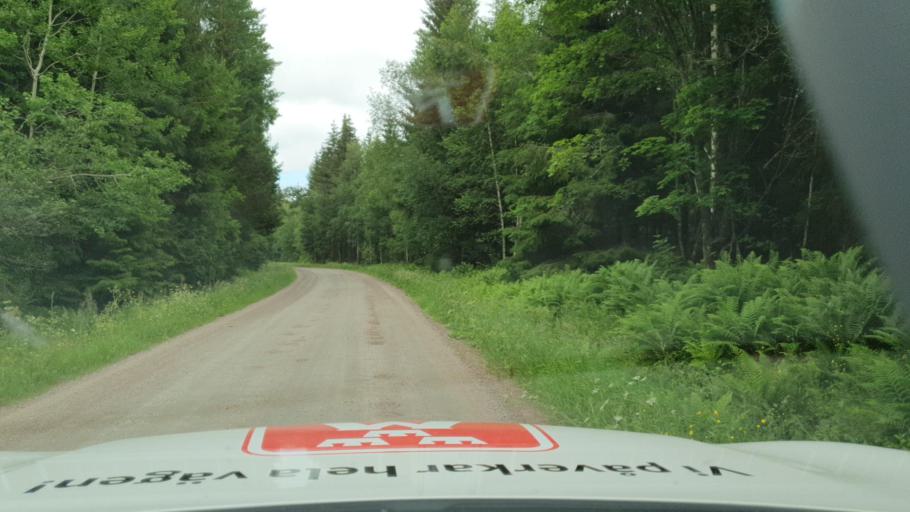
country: SE
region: Vaermland
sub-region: Filipstads Kommun
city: Filipstad
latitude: 59.5993
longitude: 13.9712
